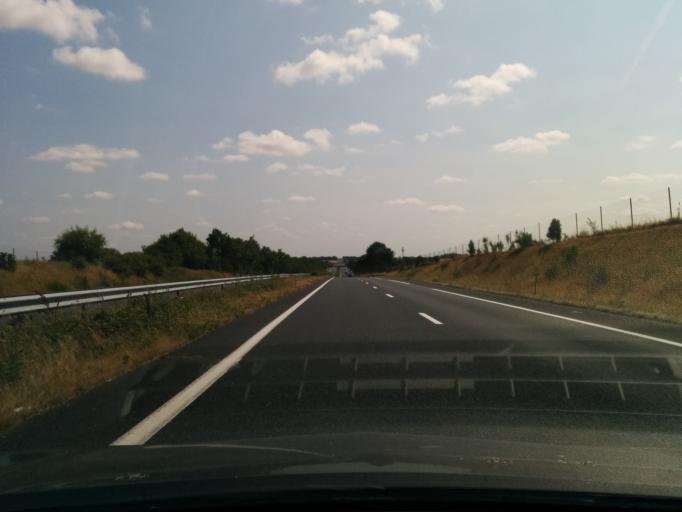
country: FR
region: Centre
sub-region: Departement de l'Indre
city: Vatan
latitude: 46.9847
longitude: 1.7701
